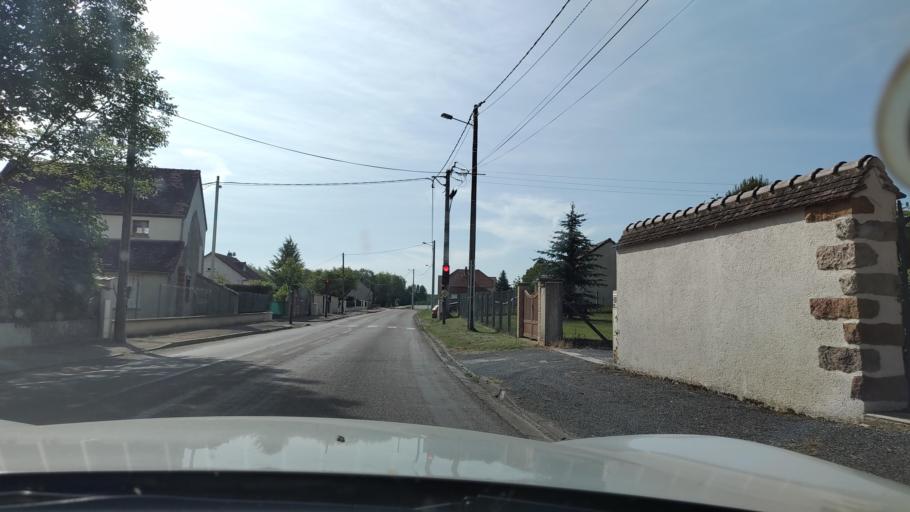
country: FR
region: Champagne-Ardenne
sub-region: Departement de l'Aube
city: Nogent-sur-Seine
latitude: 48.4728
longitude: 3.5590
